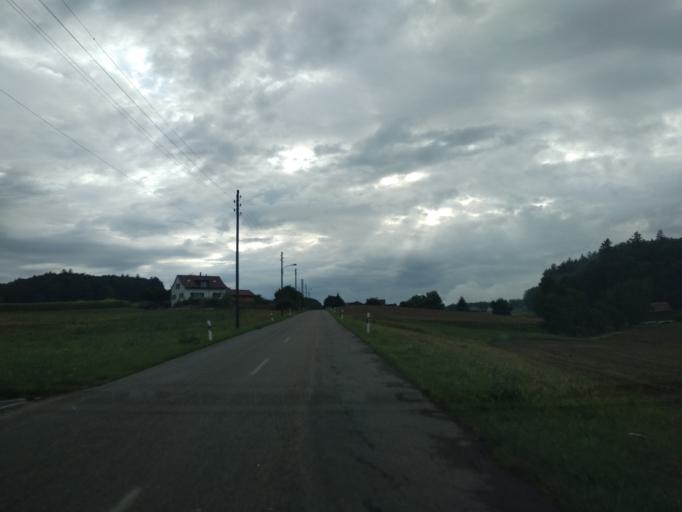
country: CH
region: Zurich
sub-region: Bezirk Andelfingen
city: Marthalen
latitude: 47.6507
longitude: 8.6711
